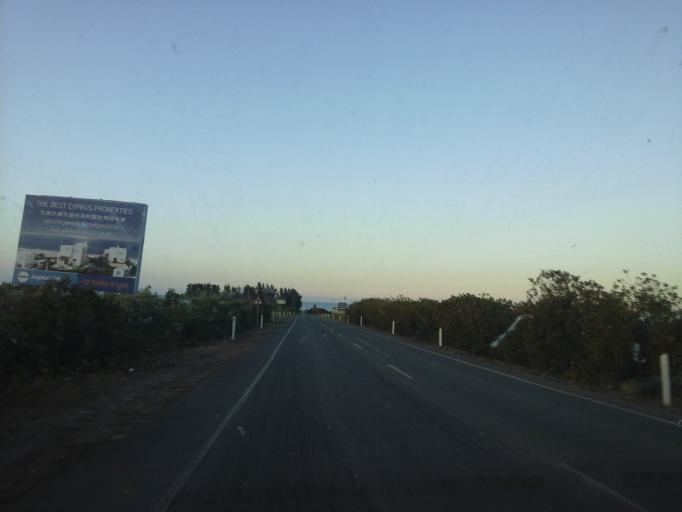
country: CY
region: Pafos
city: Paphos
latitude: 34.7239
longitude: 32.5154
